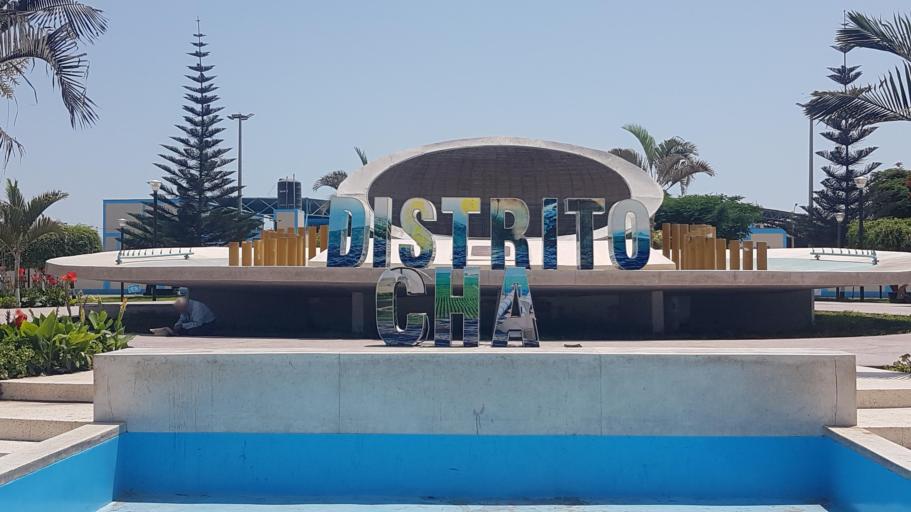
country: PE
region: La Libertad
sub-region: Viru
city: Chao
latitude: -8.5390
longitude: -78.6790
